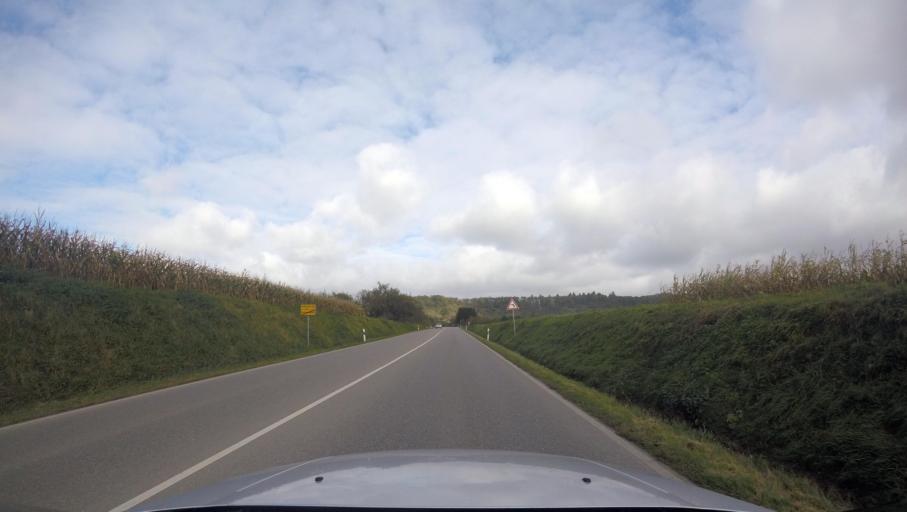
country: DE
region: Baden-Wuerttemberg
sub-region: Regierungsbezirk Stuttgart
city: Winnenden
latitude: 48.8940
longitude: 9.4240
